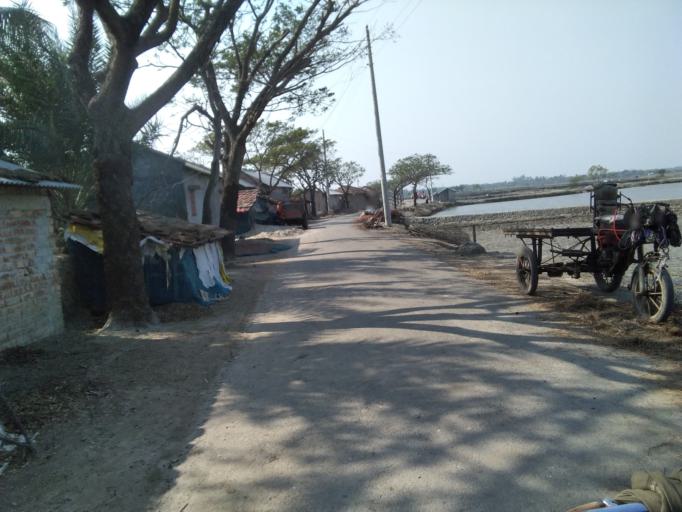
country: IN
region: West Bengal
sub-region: North 24 Parganas
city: Taki
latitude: 22.6341
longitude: 89.0117
